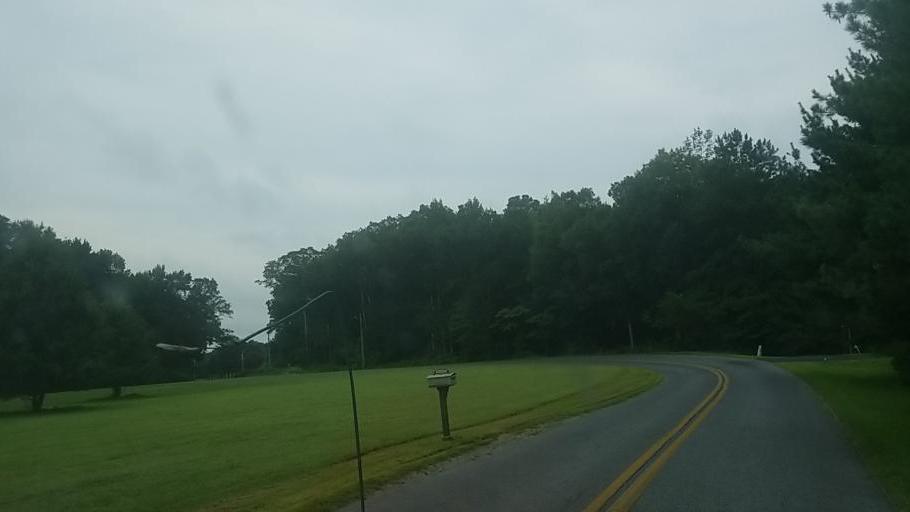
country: US
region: Maryland
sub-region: Worcester County
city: Ocean Pines
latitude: 38.4225
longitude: -75.1911
